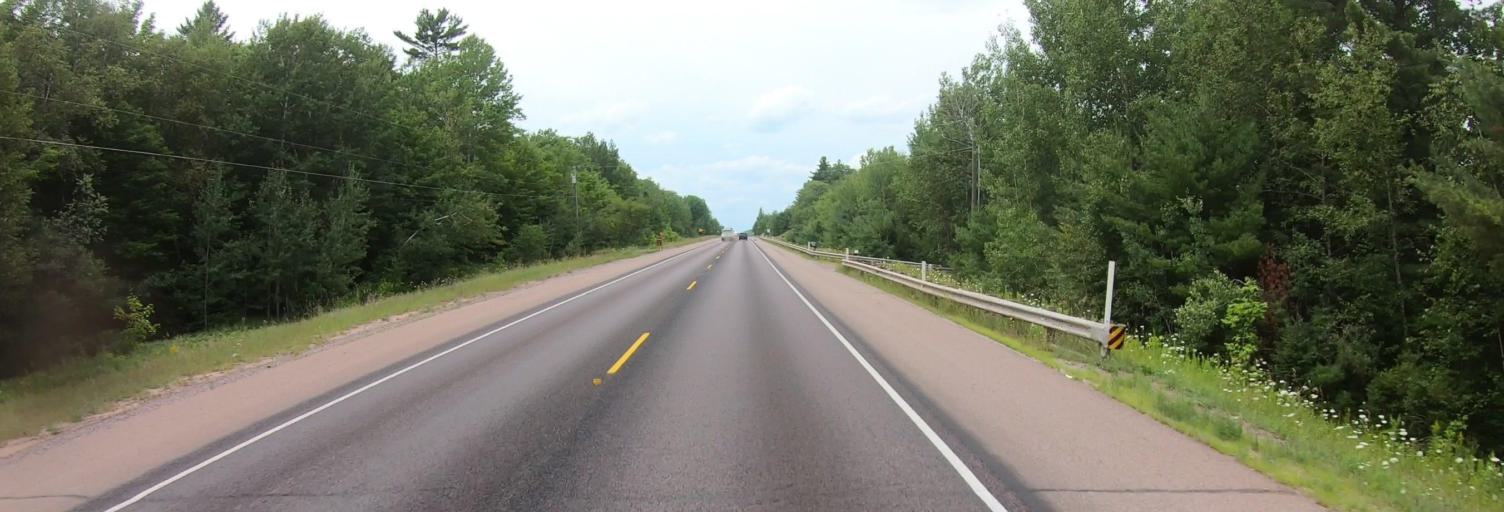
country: US
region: Michigan
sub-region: Marquette County
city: Trowbridge Park
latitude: 46.4724
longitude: -87.4452
